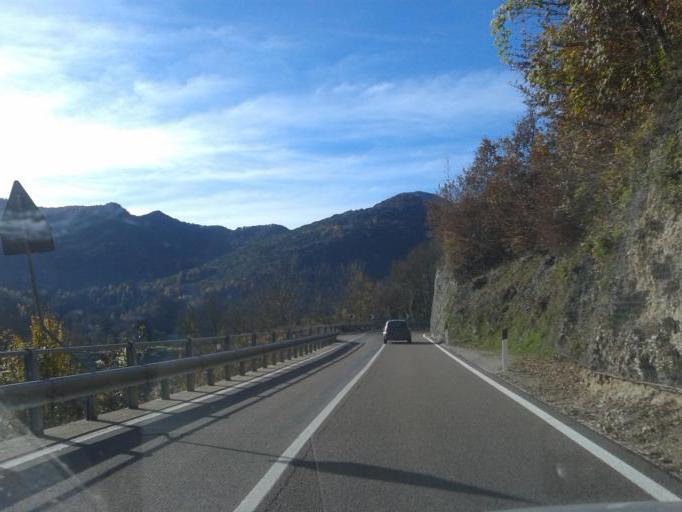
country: IT
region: Trentino-Alto Adige
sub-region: Provincia di Trento
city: Molina di Ledro
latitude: 45.8786
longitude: 10.7640
